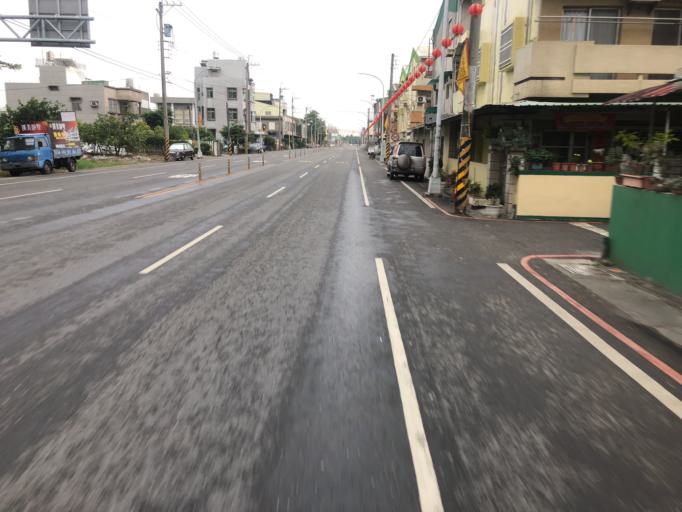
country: TW
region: Taiwan
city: Xinying
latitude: 23.1528
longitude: 120.2869
